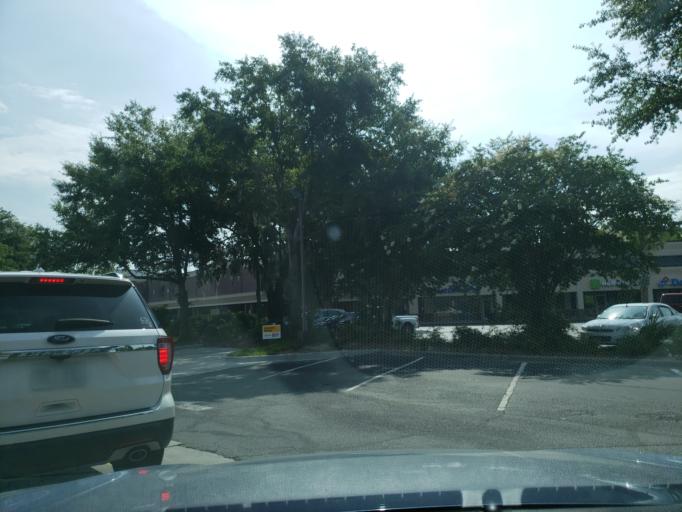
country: US
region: Georgia
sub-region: Chatham County
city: Wilmington Island
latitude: 32.0157
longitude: -80.9782
